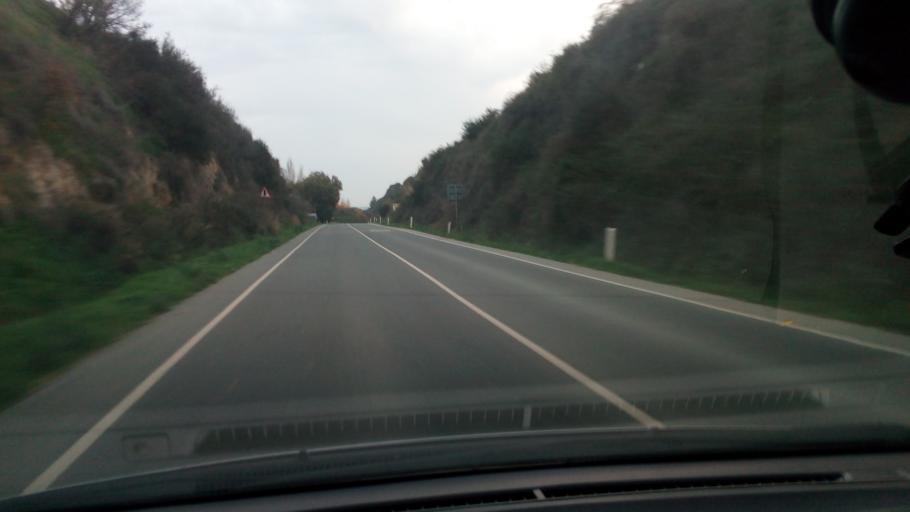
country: CY
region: Pafos
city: Polis
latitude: 34.9711
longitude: 32.4525
